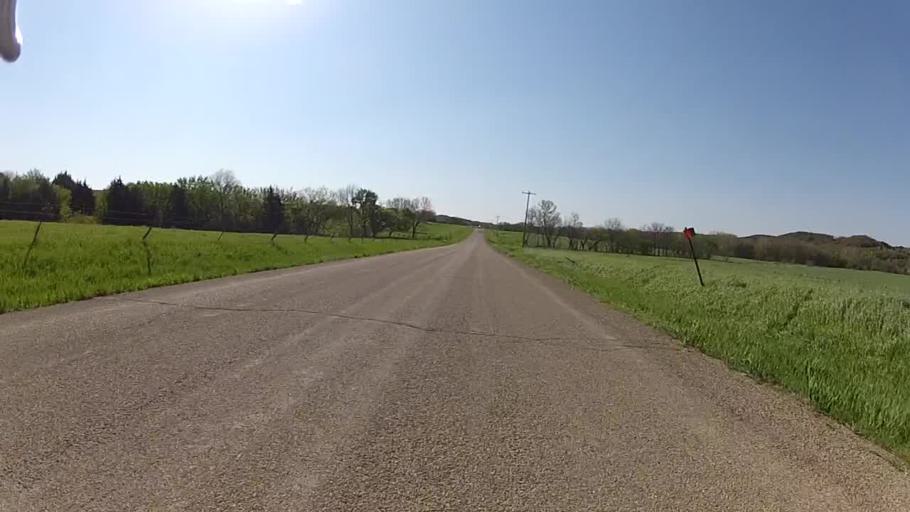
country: US
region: Kansas
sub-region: Riley County
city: Ogden
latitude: 39.0357
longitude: -96.7113
